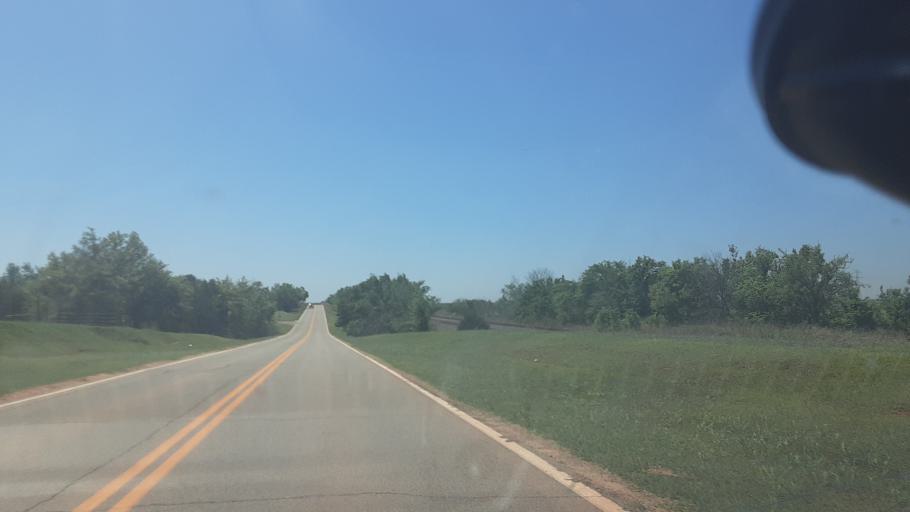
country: US
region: Oklahoma
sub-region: Logan County
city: Langston
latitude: 36.0866
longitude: -97.3973
